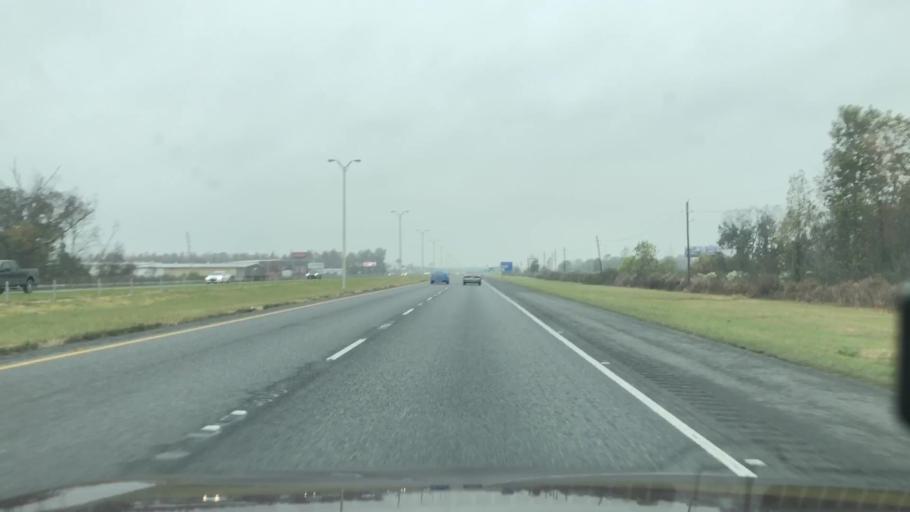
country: US
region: Louisiana
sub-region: Ouachita Parish
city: Lakeshore
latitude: 32.4927
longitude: -92.0327
